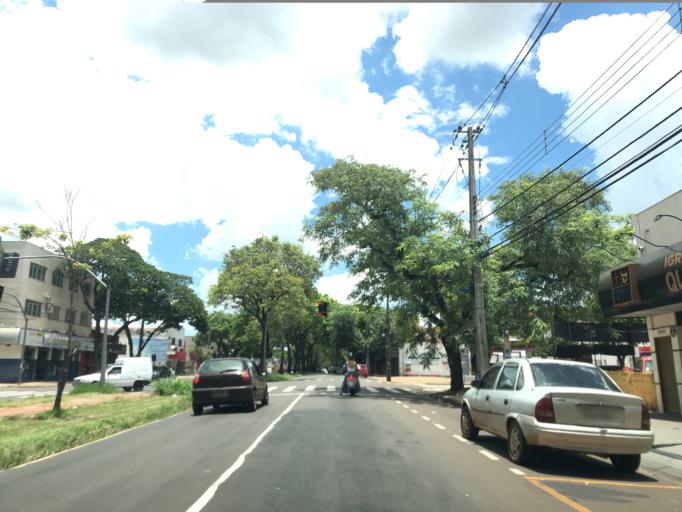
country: BR
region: Parana
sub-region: Maringa
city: Maringa
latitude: -23.4031
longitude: -51.9213
